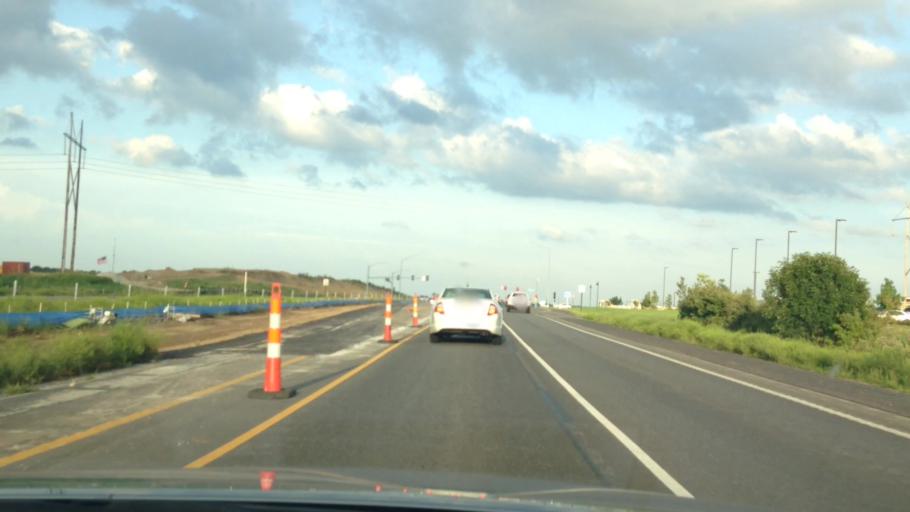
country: US
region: Missouri
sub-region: Clay County
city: Pleasant Valley
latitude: 39.2449
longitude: -94.4797
